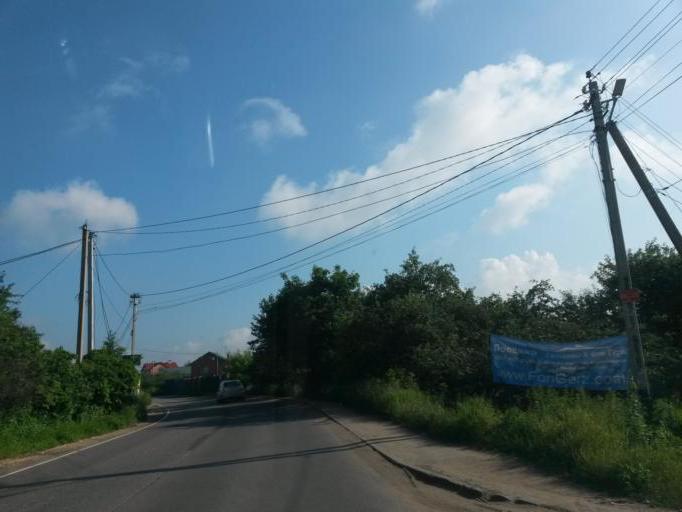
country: RU
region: Moskovskaya
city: Alekseyevka
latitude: 55.6051
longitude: 37.7914
